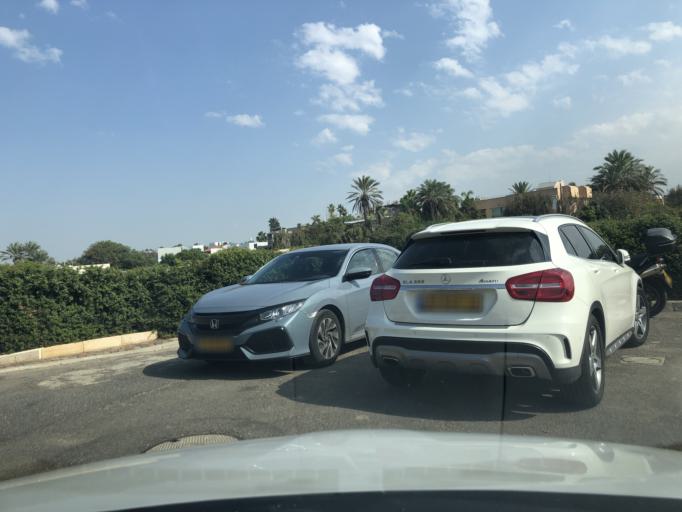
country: IL
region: Tel Aviv
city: Kefar Shemaryahu
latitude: 32.2121
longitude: 34.8149
